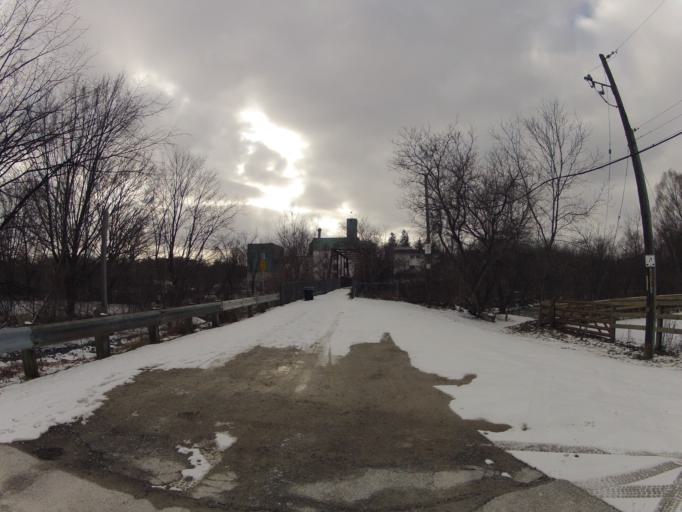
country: CA
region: Ontario
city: Mississauga
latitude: 43.5747
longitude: -79.6934
